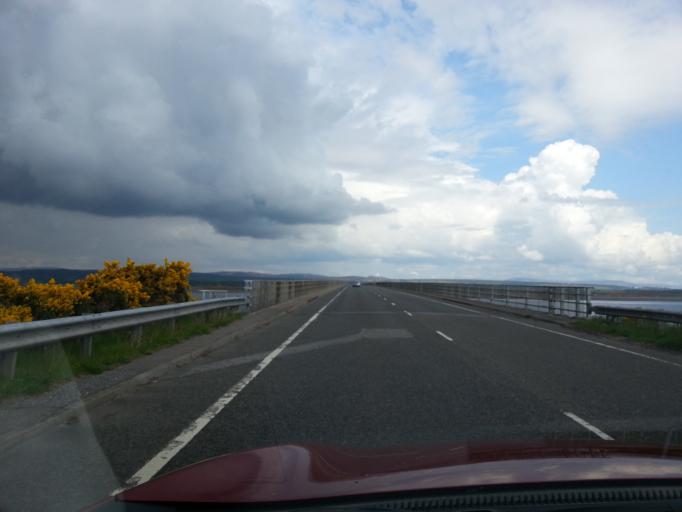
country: GB
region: Scotland
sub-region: Highland
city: Tain
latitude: 57.8405
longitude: -4.1104
